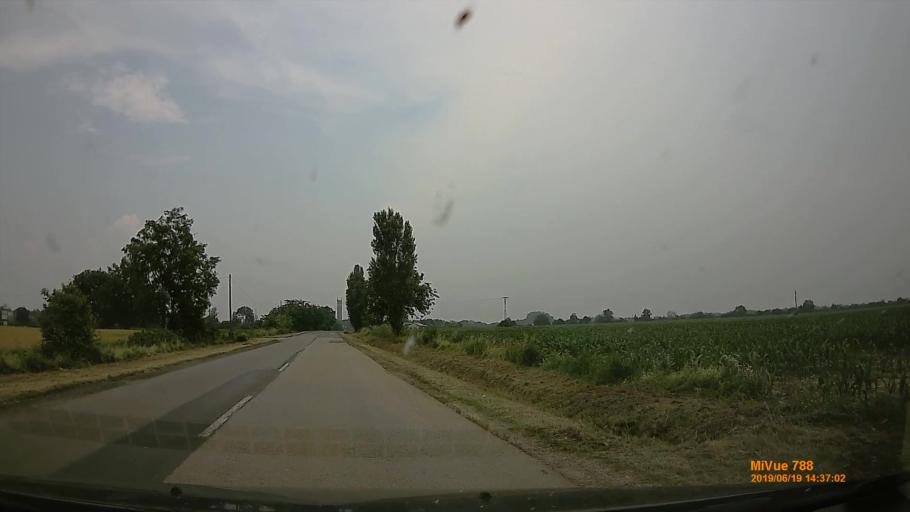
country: HU
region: Baranya
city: Szigetvar
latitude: 46.0572
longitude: 17.7785
